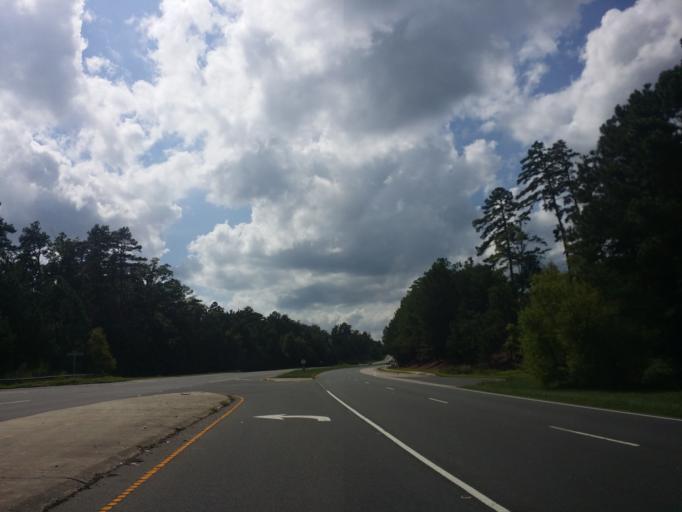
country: US
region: North Carolina
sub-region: Wake County
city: Morrisville
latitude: 35.9173
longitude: -78.7916
